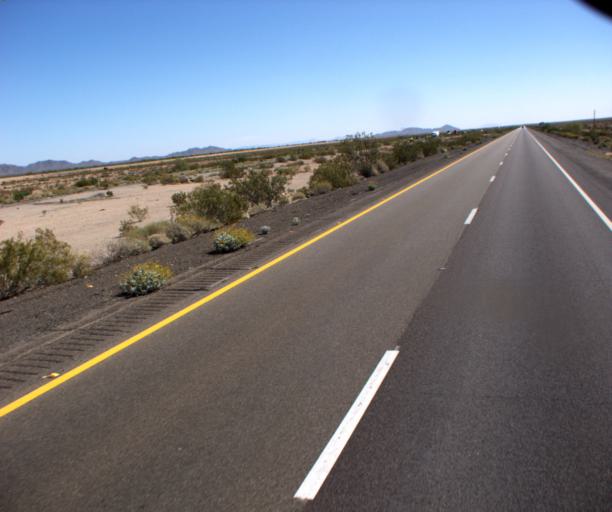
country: US
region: Arizona
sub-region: La Paz County
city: Salome
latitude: 33.6072
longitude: -113.6093
